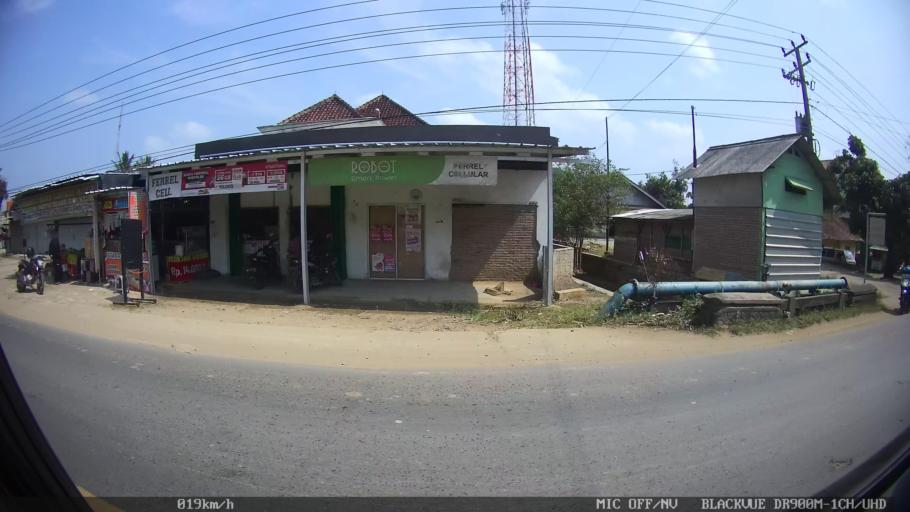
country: ID
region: Lampung
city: Gadingrejo
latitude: -5.3834
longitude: 105.0185
